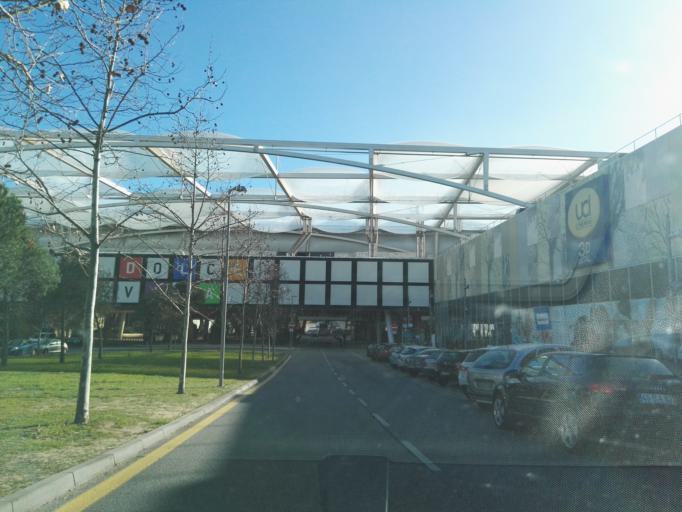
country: PT
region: Lisbon
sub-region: Odivelas
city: Famoes
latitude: 38.7781
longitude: -9.2210
